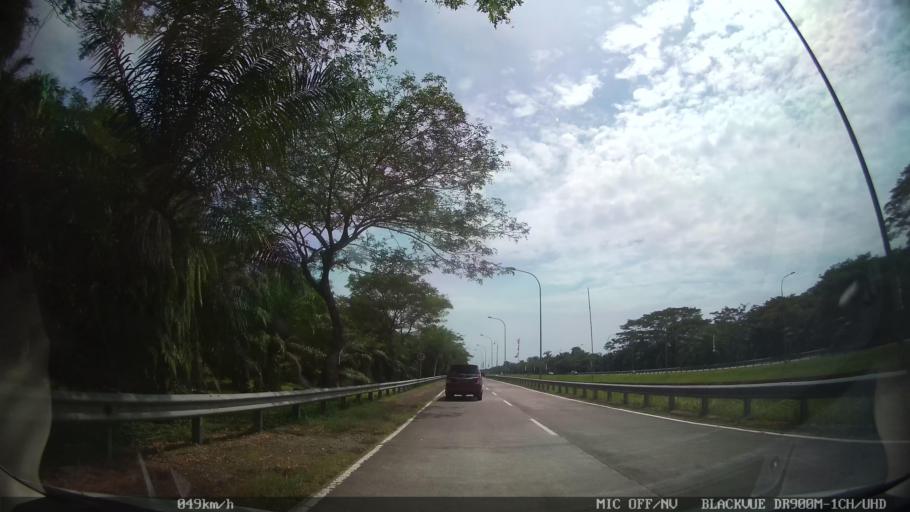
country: ID
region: North Sumatra
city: Percut
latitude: 3.6183
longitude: 98.8616
